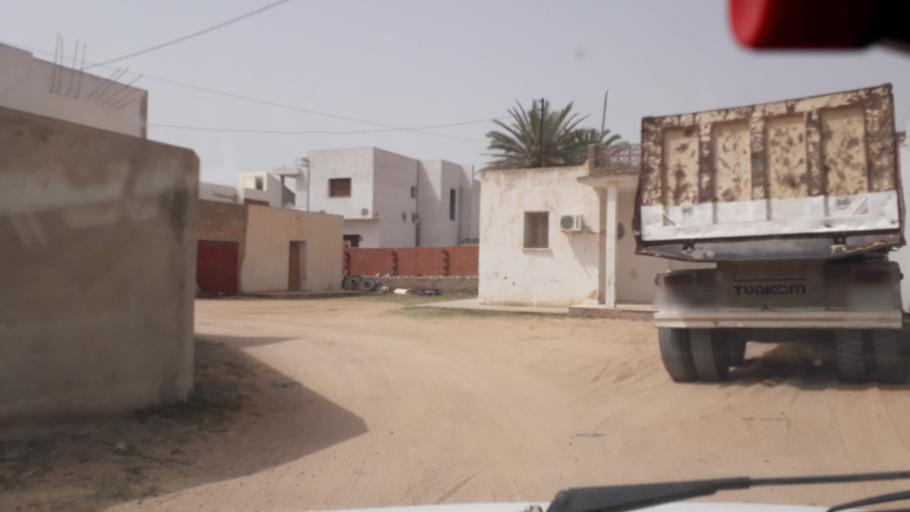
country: TN
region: Safaqis
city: Al Qarmadah
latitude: 34.8071
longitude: 10.7734
